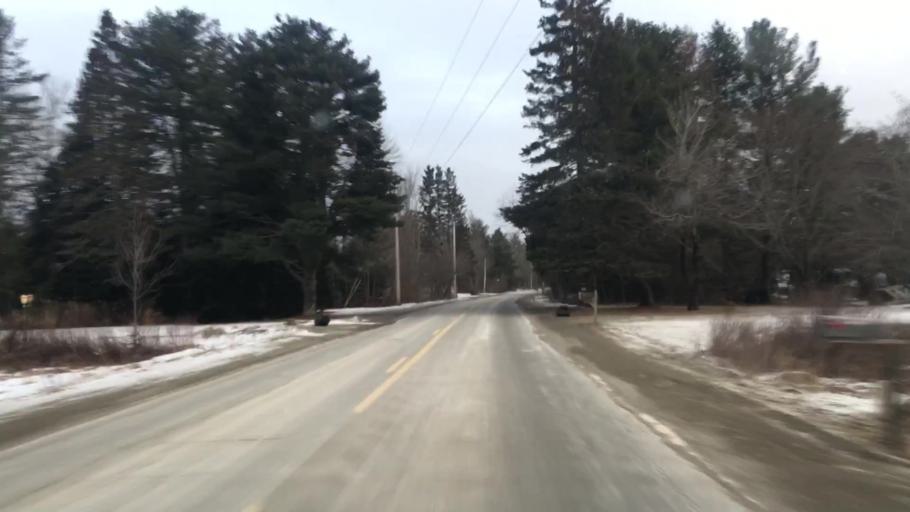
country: US
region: Maine
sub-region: Hancock County
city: Franklin
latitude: 44.6885
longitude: -68.3492
